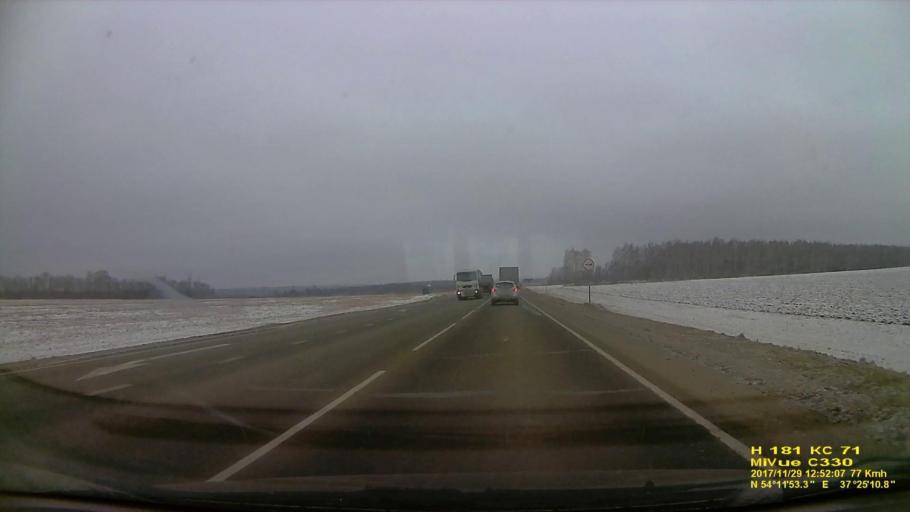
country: RU
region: Tula
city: Barsuki
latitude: 54.1982
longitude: 37.4195
